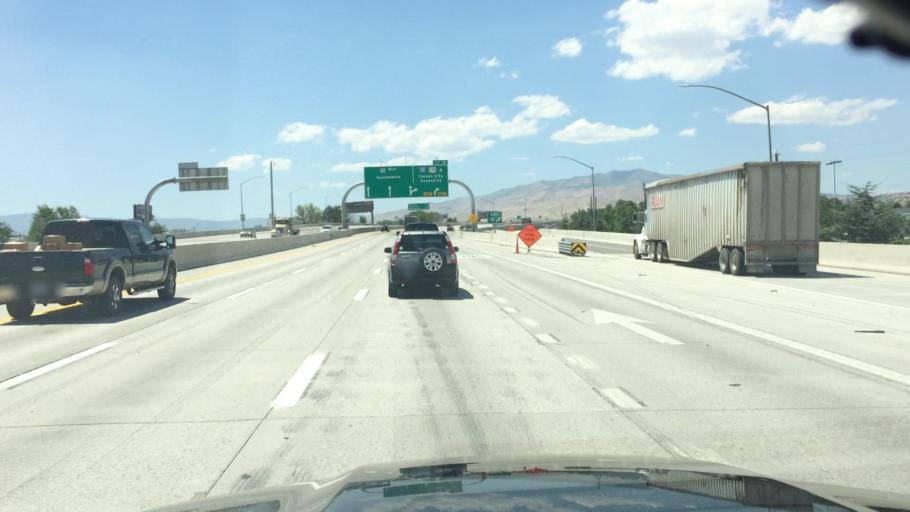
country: US
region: Nevada
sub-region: Washoe County
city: Sparks
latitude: 39.5343
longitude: -119.7738
